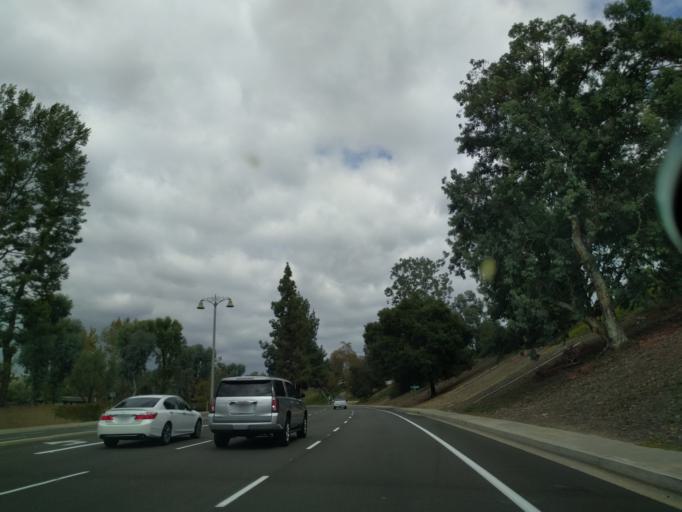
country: US
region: California
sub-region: Orange County
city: Mission Viejo
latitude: 33.6268
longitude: -117.6694
